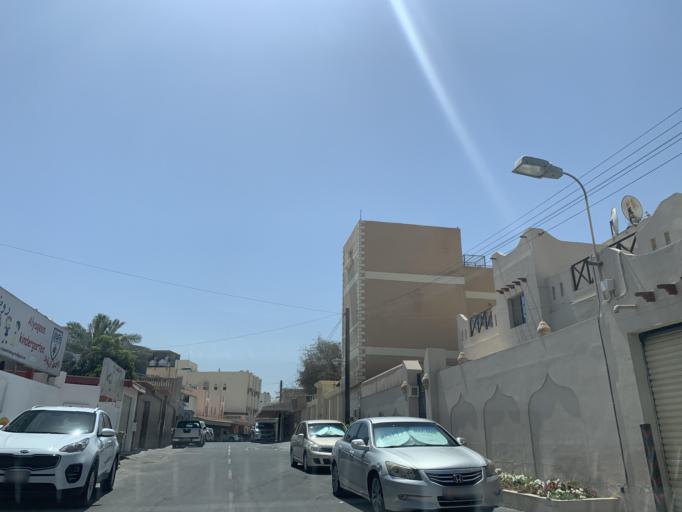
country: BH
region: Northern
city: Ar Rifa'
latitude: 26.1341
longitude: 50.5771
